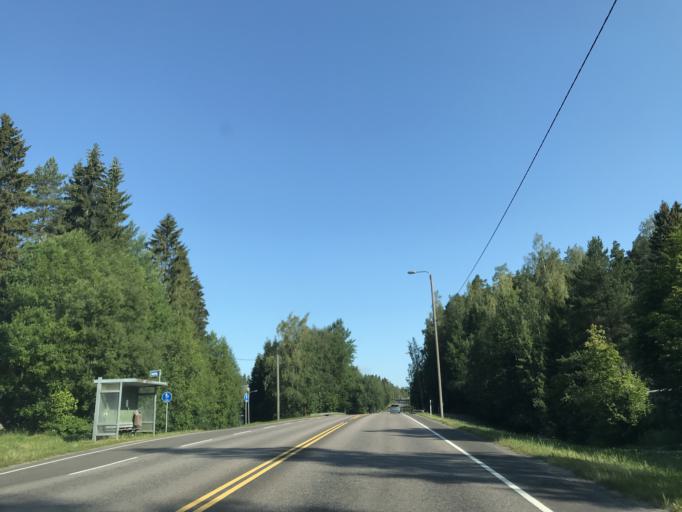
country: FI
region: Paijanne Tavastia
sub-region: Lahti
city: Lahti
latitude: 61.0336
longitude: 25.6717
